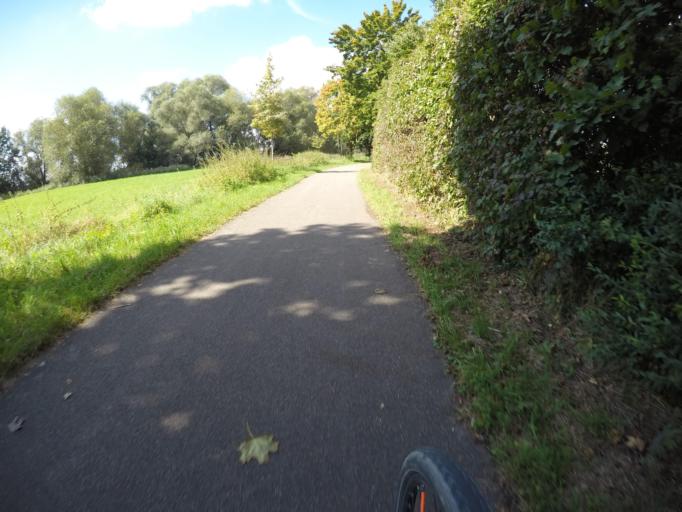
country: DE
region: Bavaria
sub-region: Swabia
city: Wittislingen
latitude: 48.6073
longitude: 10.4493
